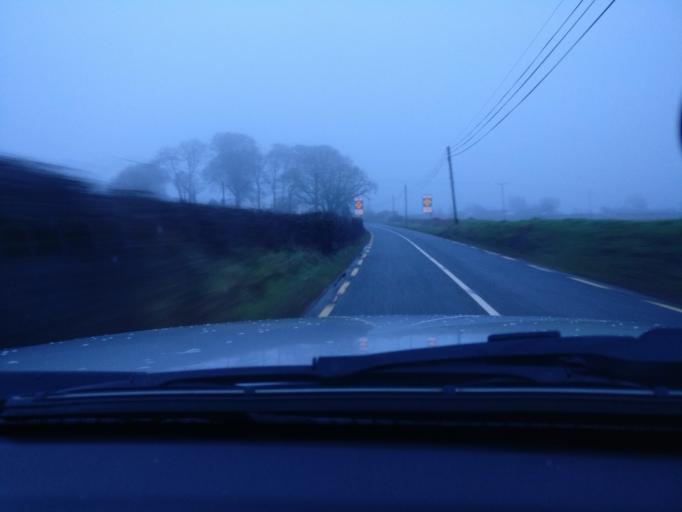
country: IE
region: Leinster
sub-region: An Mhi
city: Athboy
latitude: 53.6170
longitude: -6.9365
